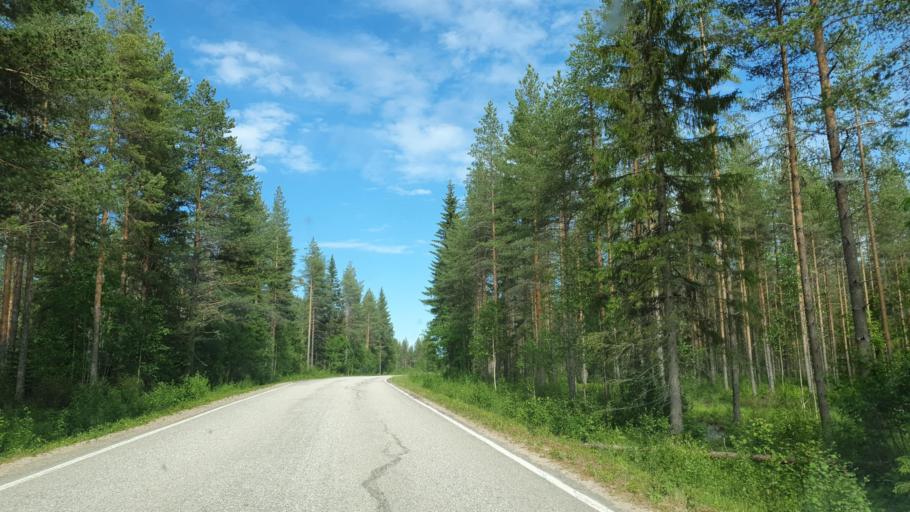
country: FI
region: Kainuu
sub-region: Kehys-Kainuu
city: Suomussalmi
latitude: 64.5787
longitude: 29.0369
